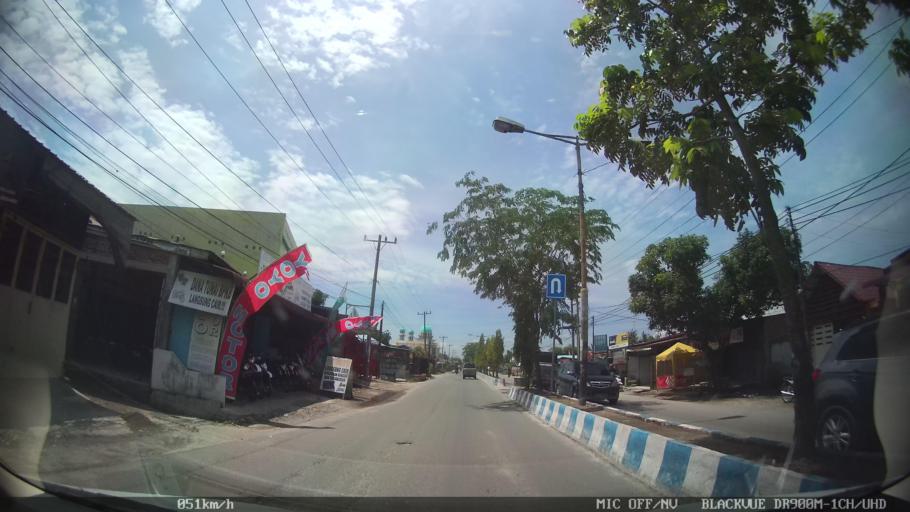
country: ID
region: North Sumatra
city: Percut
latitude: 3.5516
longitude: 98.8796
